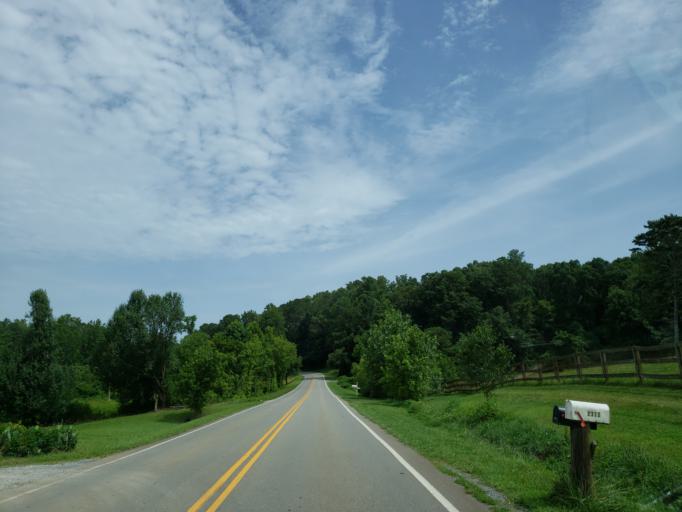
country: US
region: Georgia
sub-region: Pickens County
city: Jasper
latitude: 34.4499
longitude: -84.4392
